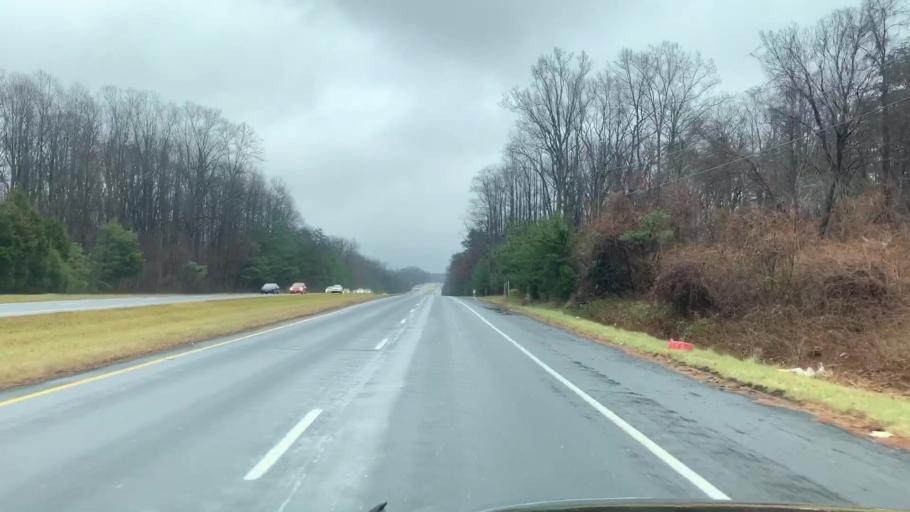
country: US
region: Virginia
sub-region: Fairfax County
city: Fairfax Station
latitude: 38.7760
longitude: -77.3250
